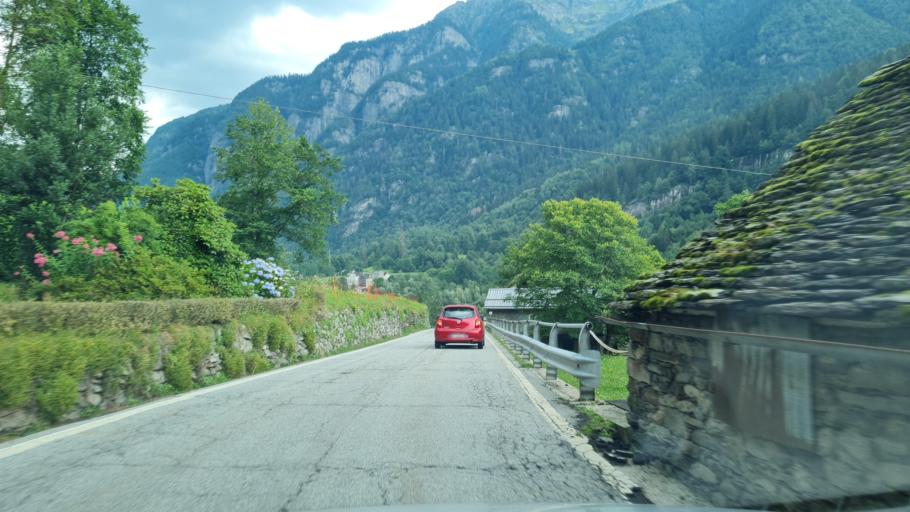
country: IT
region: Piedmont
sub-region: Provincia Verbano-Cusio-Ossola
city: Premia
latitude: 46.2766
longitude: 8.3486
